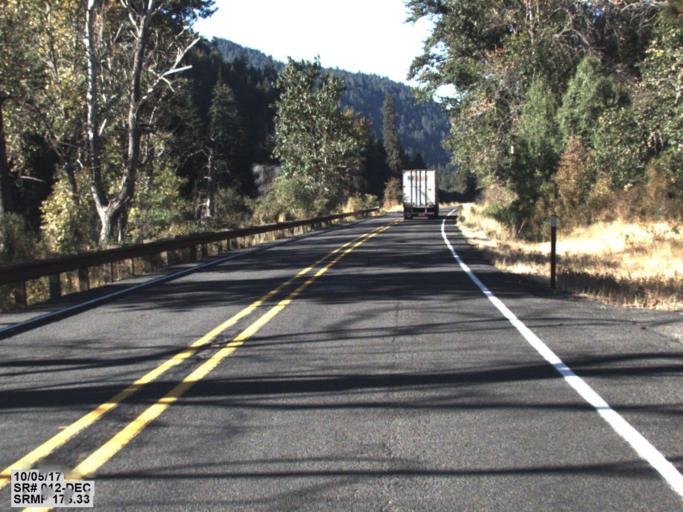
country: US
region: Washington
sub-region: Yakima County
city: Tieton
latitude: 46.6895
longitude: -120.9253
